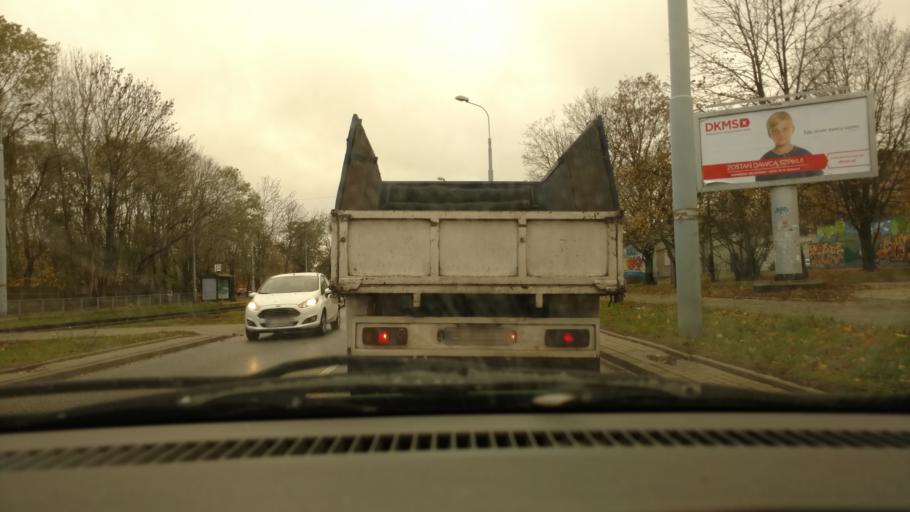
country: PL
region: Lodz Voivodeship
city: Lodz
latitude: 51.7777
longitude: 19.4958
